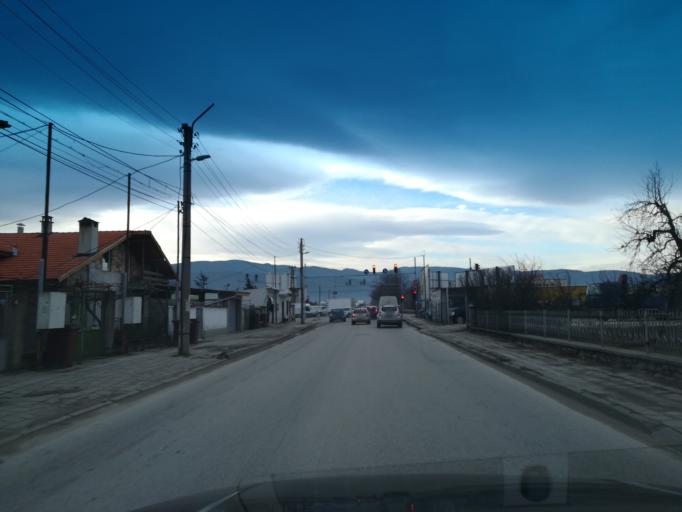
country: BG
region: Plovdiv
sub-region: Obshtina Plovdiv
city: Plovdiv
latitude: 42.0968
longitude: 24.6984
